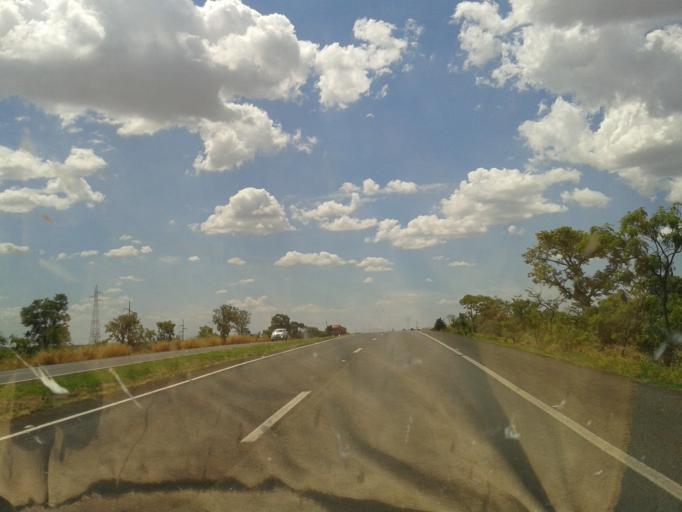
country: BR
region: Minas Gerais
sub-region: Uberlandia
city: Uberlandia
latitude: -19.1012
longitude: -48.1811
